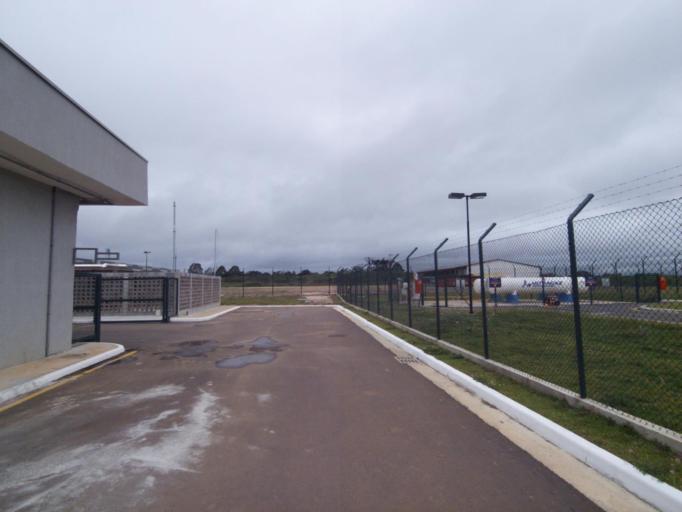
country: BR
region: Parana
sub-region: Sao Jose Dos Pinhais
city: Sao Jose dos Pinhais
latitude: -25.5376
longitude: -49.1721
